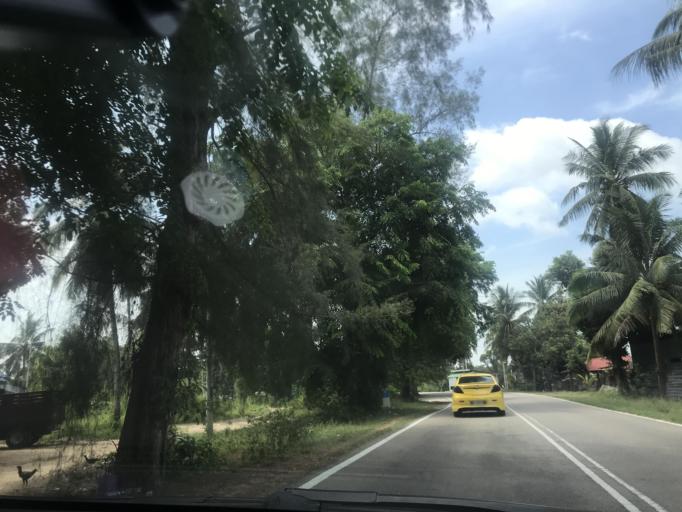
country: MY
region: Kelantan
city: Tumpat
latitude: 6.2082
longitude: 102.1414
